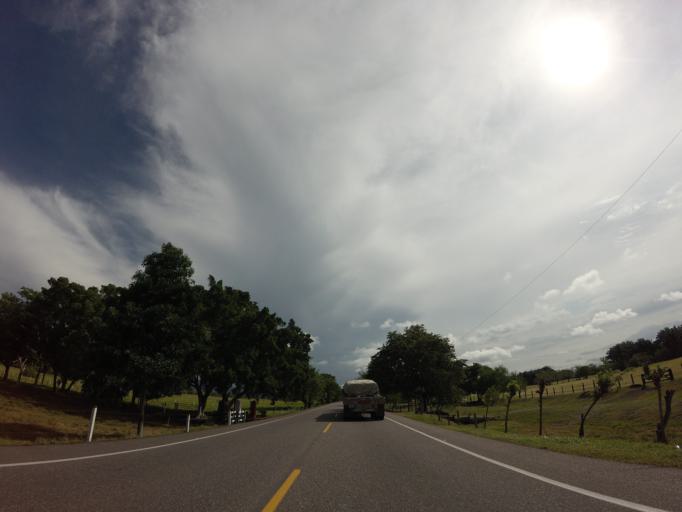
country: CO
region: Tolima
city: Honda
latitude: 5.3269
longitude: -74.7396
